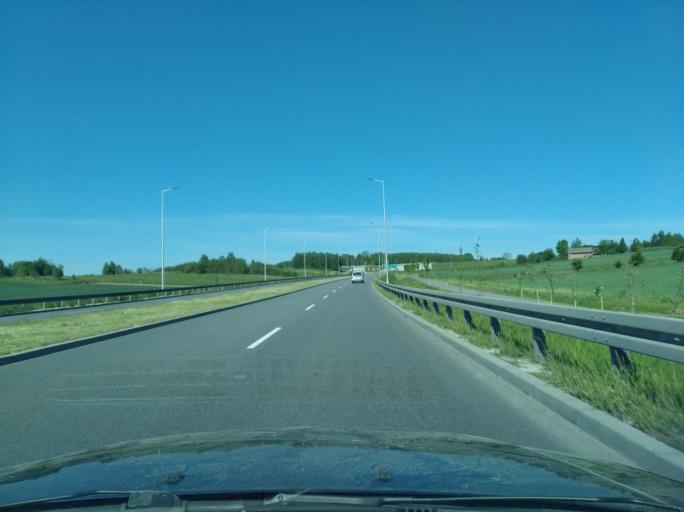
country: PL
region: Subcarpathian Voivodeship
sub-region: Powiat rzeszowski
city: Kielanowka
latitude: 50.0140
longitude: 21.9298
